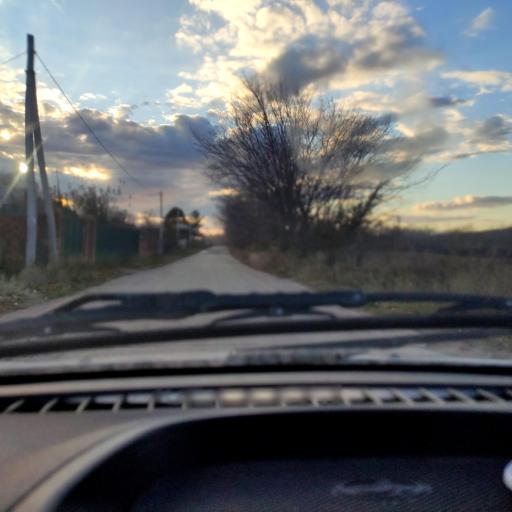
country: RU
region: Samara
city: Povolzhskiy
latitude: 53.4650
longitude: 49.6737
